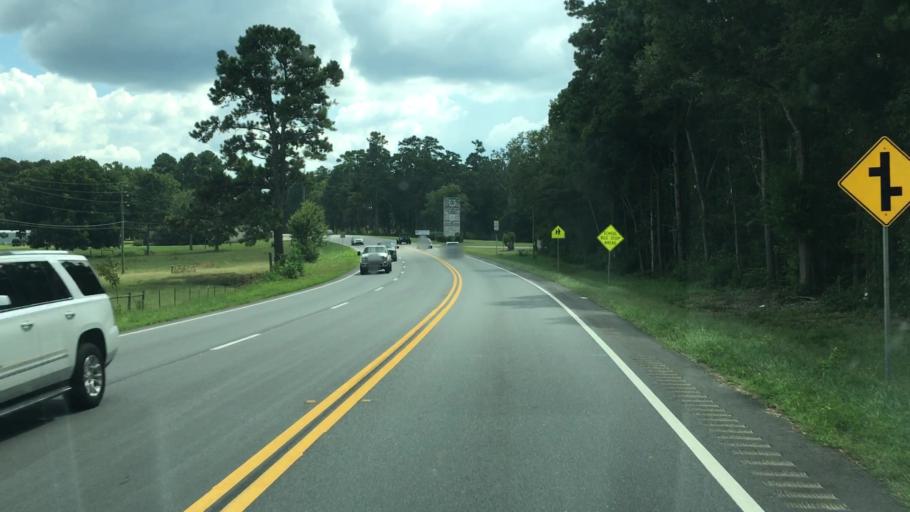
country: US
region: Georgia
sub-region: Putnam County
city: Jefferson
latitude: 33.4193
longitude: -83.3721
